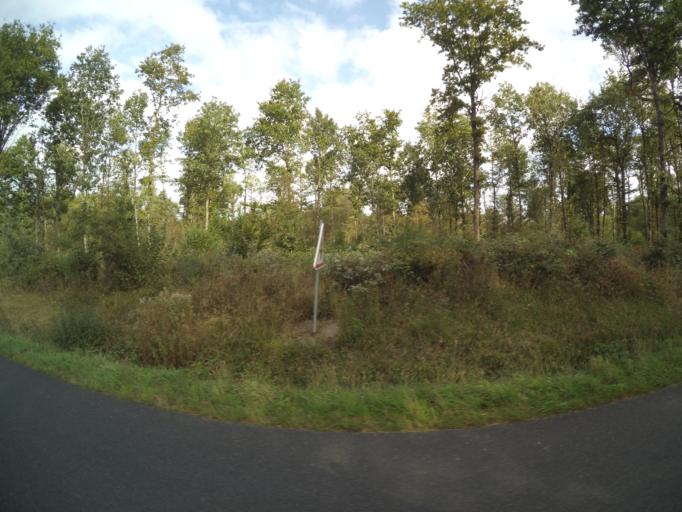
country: FR
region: Centre
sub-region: Departement d'Indre-et-Loire
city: Nazelles-Negron
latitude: 47.4607
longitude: 0.9547
